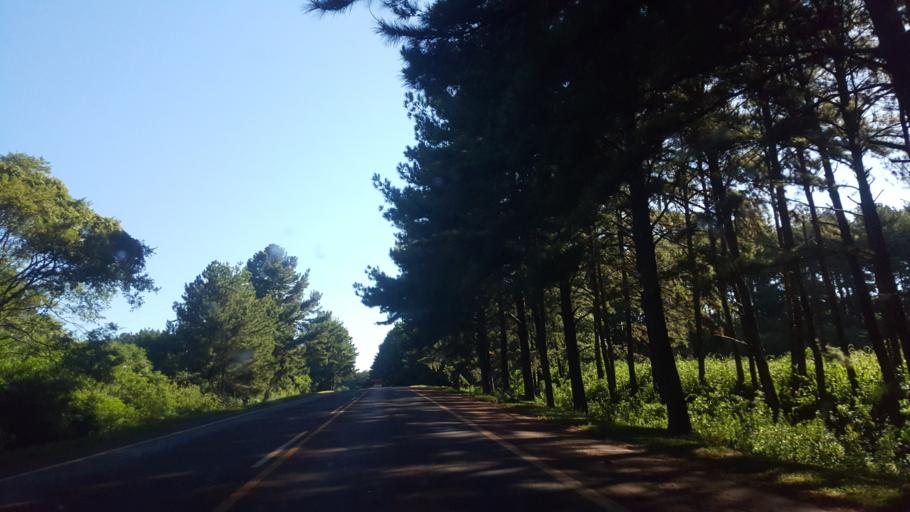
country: AR
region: Misiones
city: Puerto Libertad
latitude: -25.9048
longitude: -54.5646
